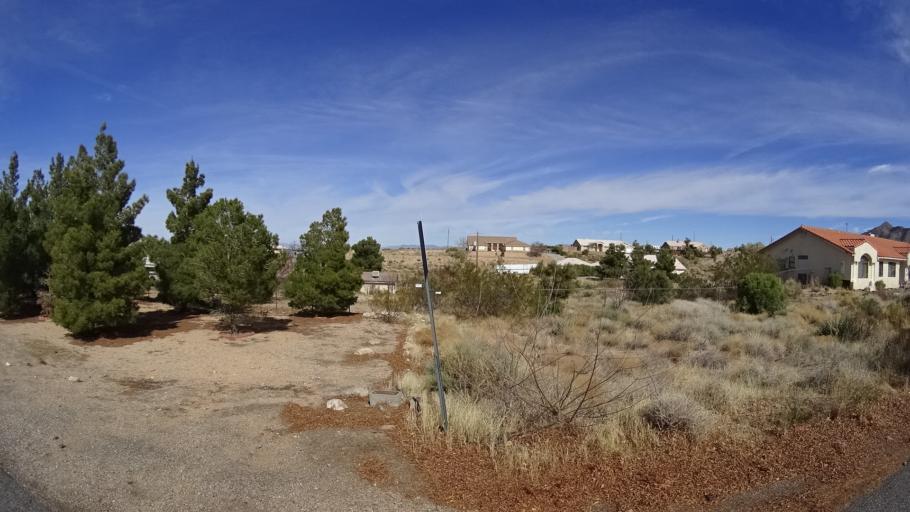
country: US
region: Arizona
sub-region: Mohave County
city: Kingman
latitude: 35.1783
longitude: -113.9896
